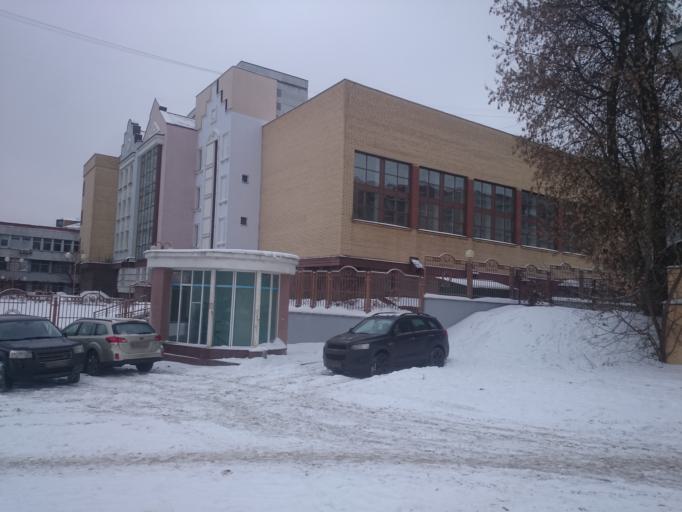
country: RU
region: Moscow
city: Lefortovo
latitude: 55.7715
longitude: 37.6882
